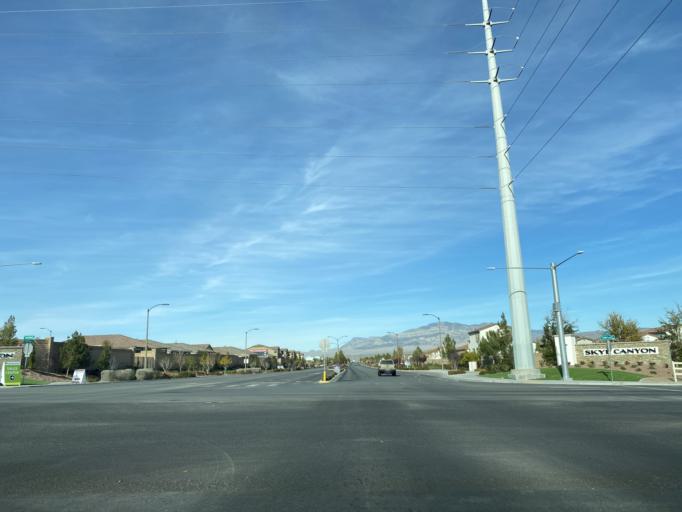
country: US
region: Nevada
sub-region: Clark County
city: Summerlin South
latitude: 36.3067
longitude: -115.3149
